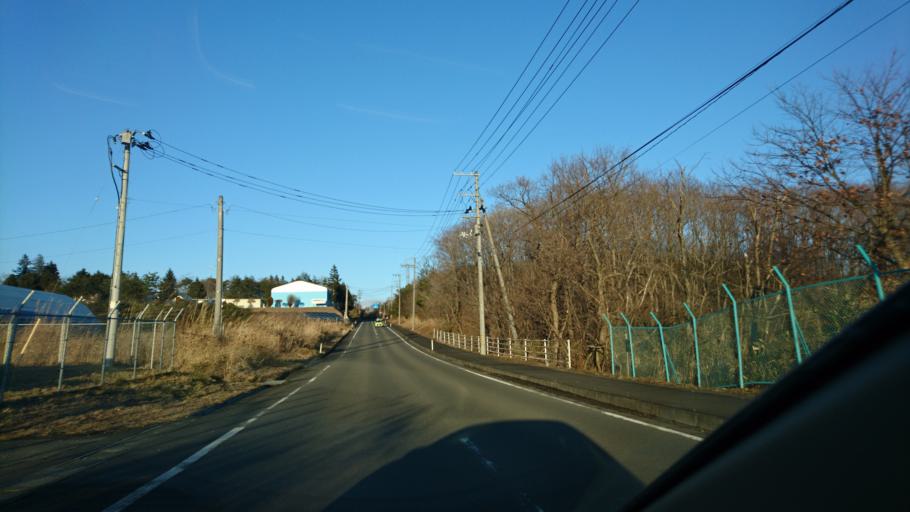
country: JP
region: Miyagi
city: Furukawa
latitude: 38.6672
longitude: 140.9052
